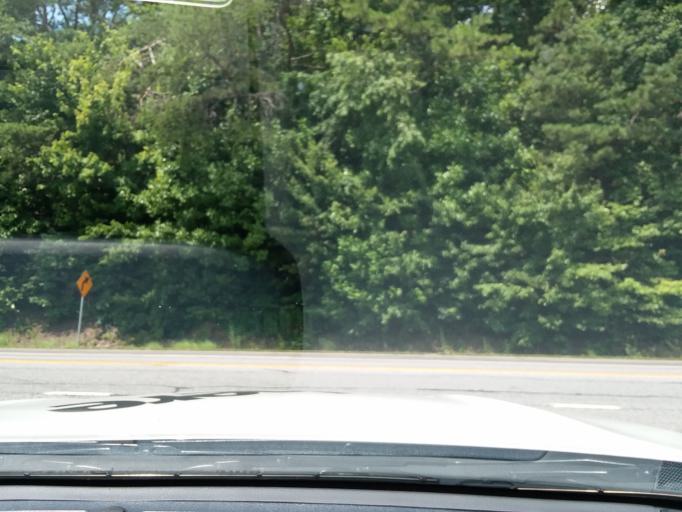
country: US
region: Georgia
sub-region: Rabun County
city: Mountain City
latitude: 34.9792
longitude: -83.3837
